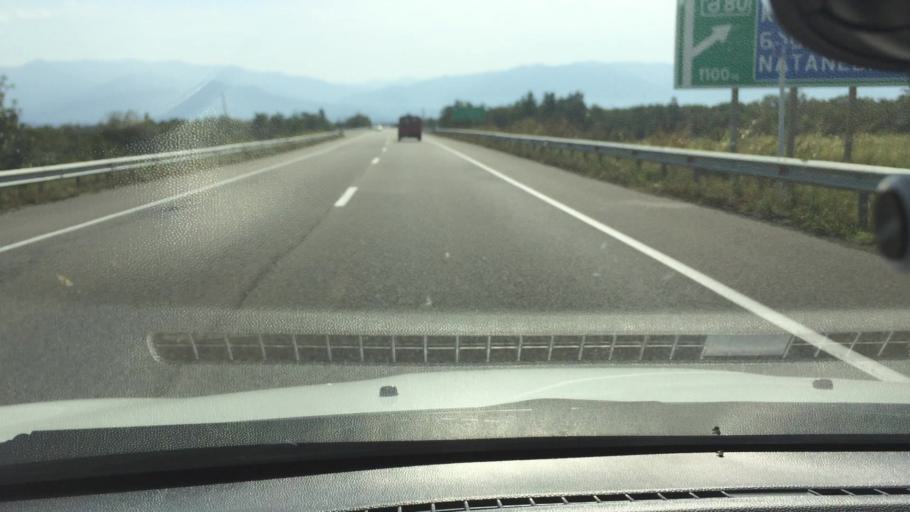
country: GE
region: Guria
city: Urek'i
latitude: 41.9109
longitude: 41.7820
